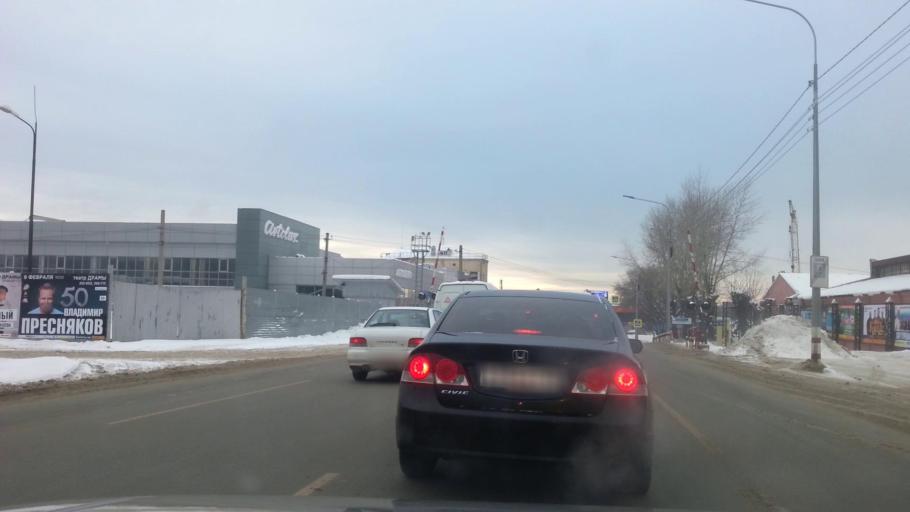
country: RU
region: Altai Krai
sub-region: Gorod Barnaulskiy
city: Barnaul
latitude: 53.3407
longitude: 83.7451
